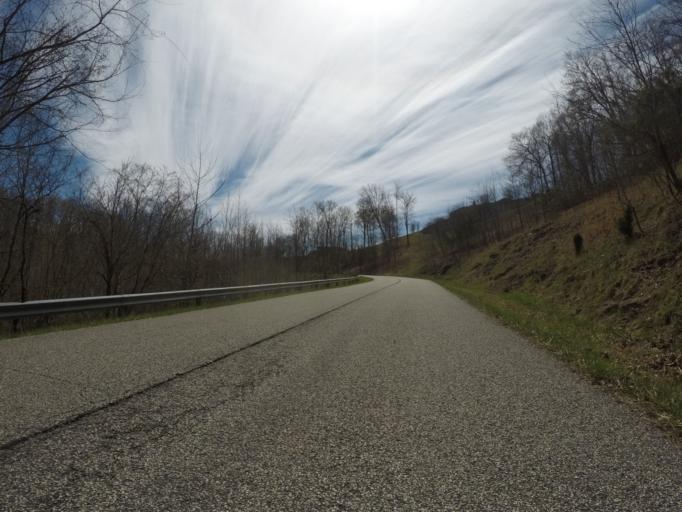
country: US
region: West Virginia
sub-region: Cabell County
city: Barboursville
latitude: 38.4040
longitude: -82.3079
